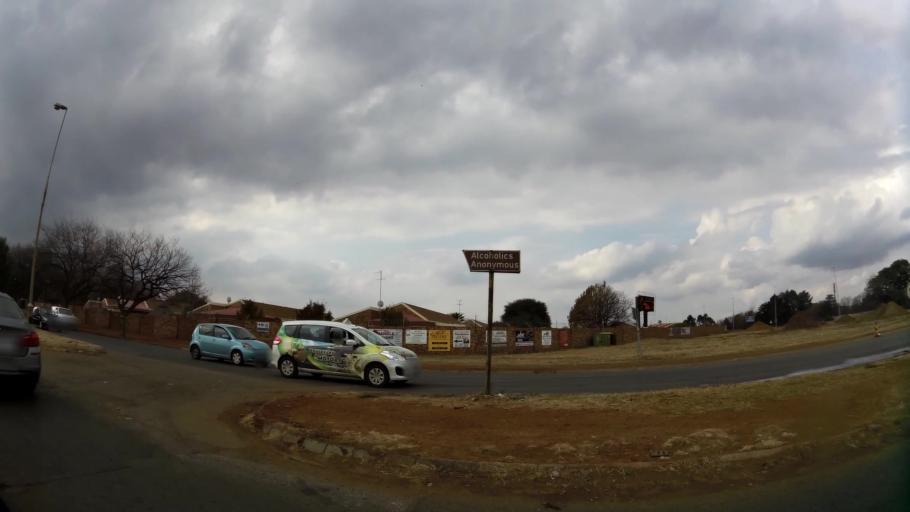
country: ZA
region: Gauteng
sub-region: Sedibeng District Municipality
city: Vanderbijlpark
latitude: -26.7066
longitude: 27.8243
